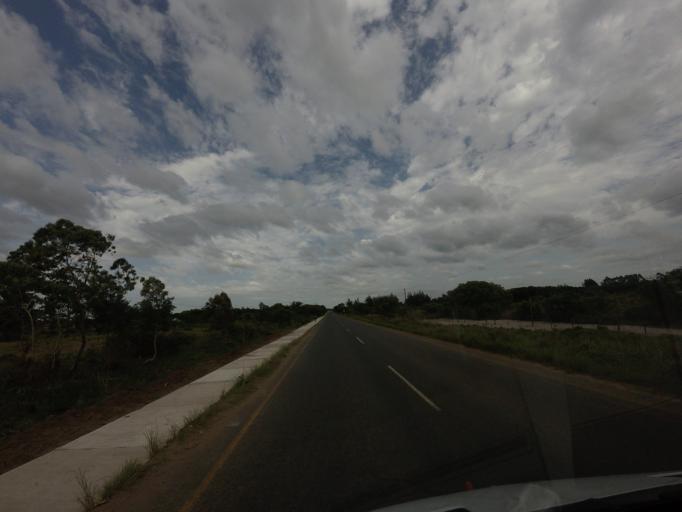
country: ZA
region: KwaZulu-Natal
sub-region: uMkhanyakude District Municipality
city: Mtubatuba
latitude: -28.3752
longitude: 32.3829
